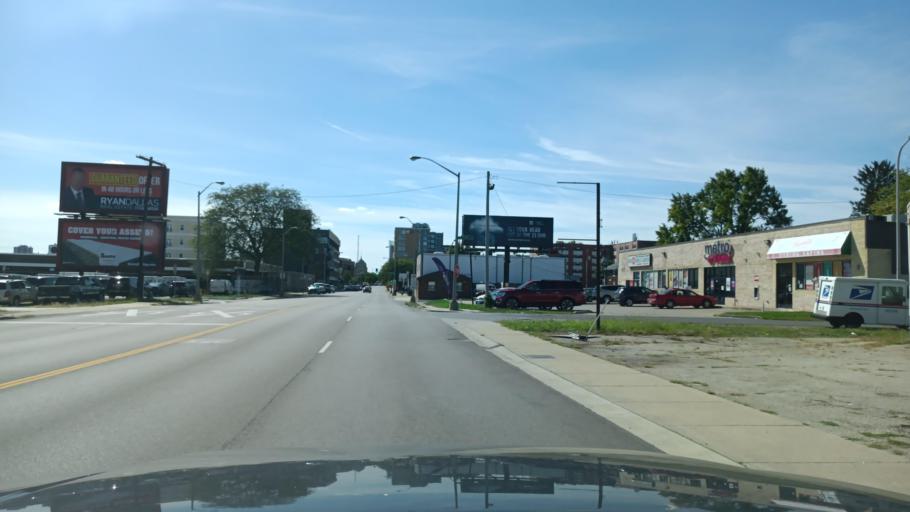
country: US
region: Illinois
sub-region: Champaign County
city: Champaign
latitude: 40.1230
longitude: -88.2436
